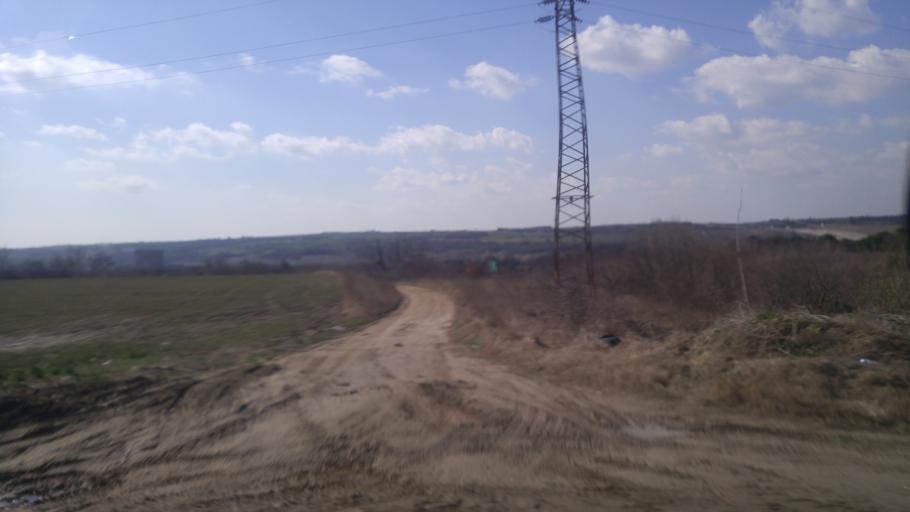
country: TR
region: Istanbul
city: Buyukcavuslu
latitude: 41.1981
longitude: 28.0807
